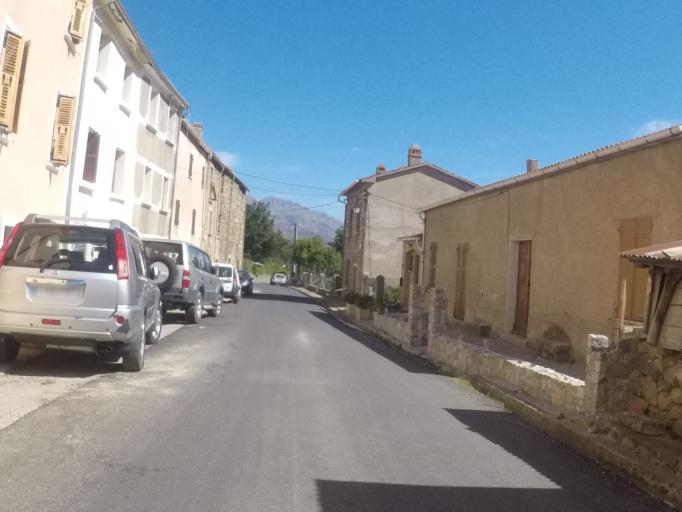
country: FR
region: Corsica
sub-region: Departement de la Haute-Corse
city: Corte
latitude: 42.3187
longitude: 9.0029
